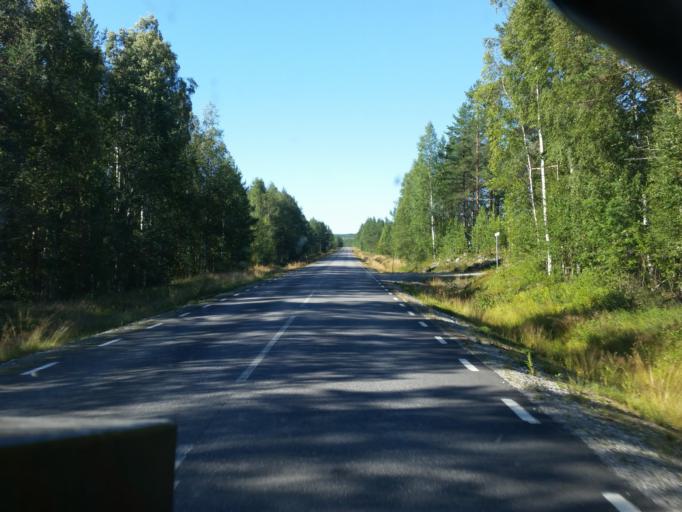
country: SE
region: Norrbotten
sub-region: Pitea Kommun
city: Roknas
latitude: 65.1942
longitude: 21.0940
